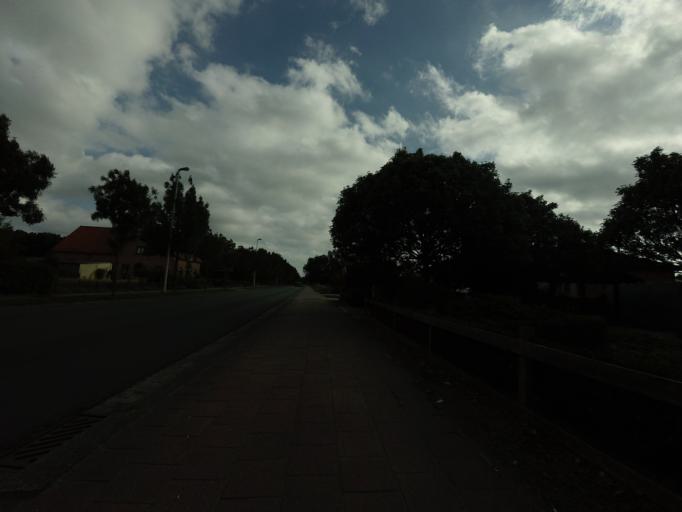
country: BE
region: Flanders
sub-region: Provincie Antwerpen
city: Boom
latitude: 51.1100
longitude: 4.3830
